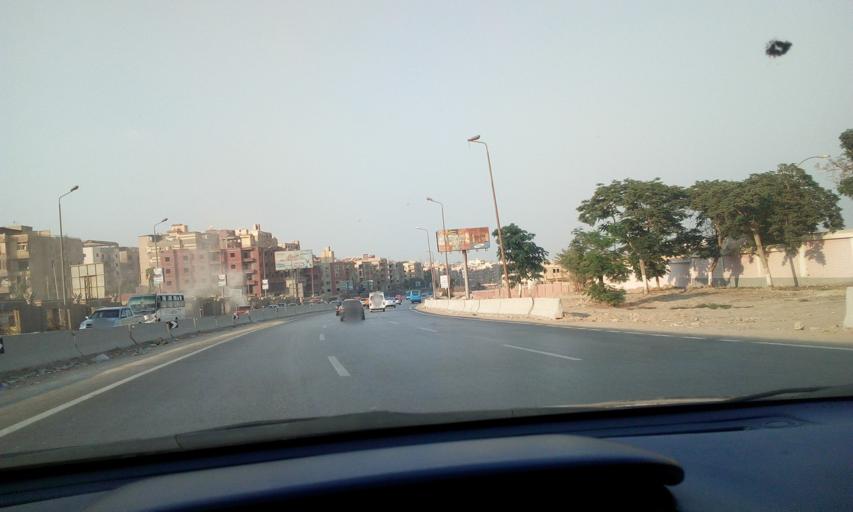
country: EG
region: Al Jizah
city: Al Jizah
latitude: 29.9698
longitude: 31.1083
